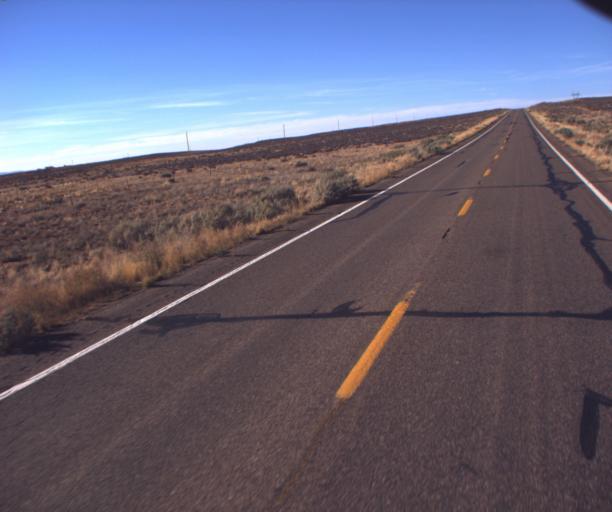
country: US
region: Arizona
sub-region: Coconino County
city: LeChee
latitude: 36.7885
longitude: -111.2950
